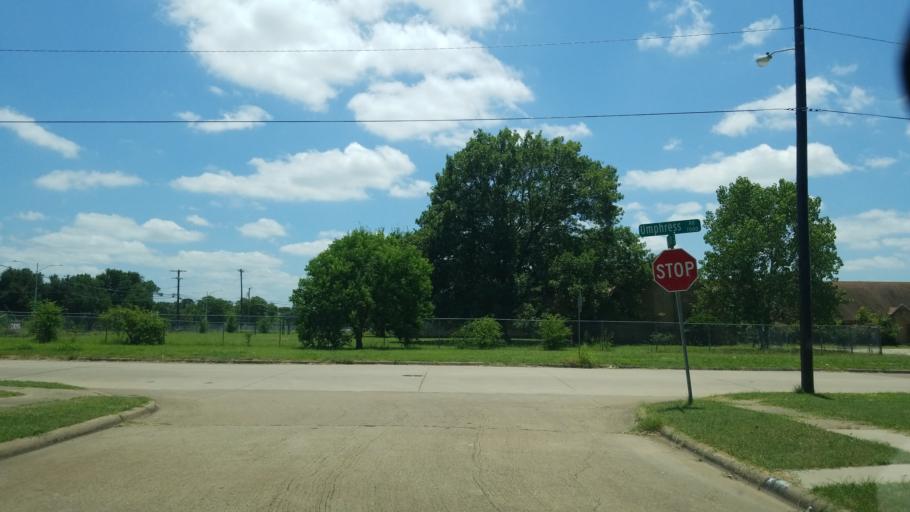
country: US
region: Texas
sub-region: Dallas County
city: Balch Springs
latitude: 32.7417
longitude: -96.7008
